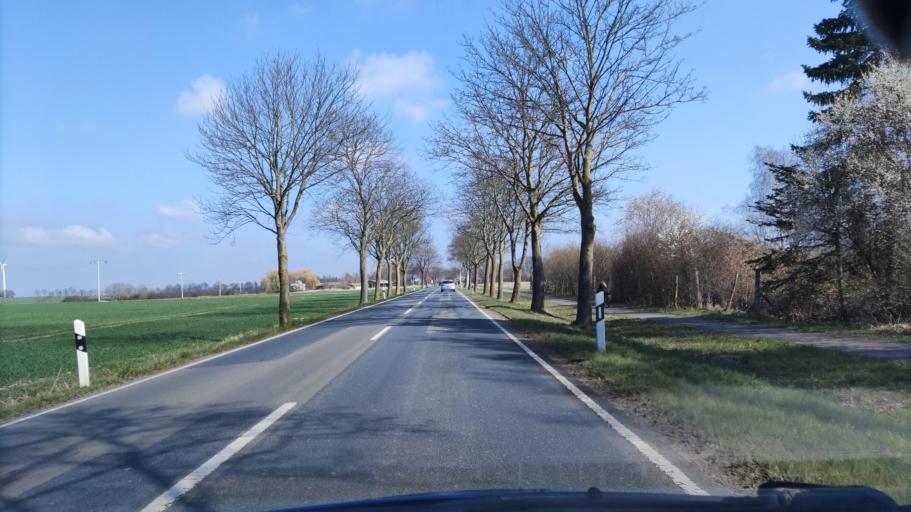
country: DE
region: Lower Saxony
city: Wustrow
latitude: 52.9445
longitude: 11.1272
